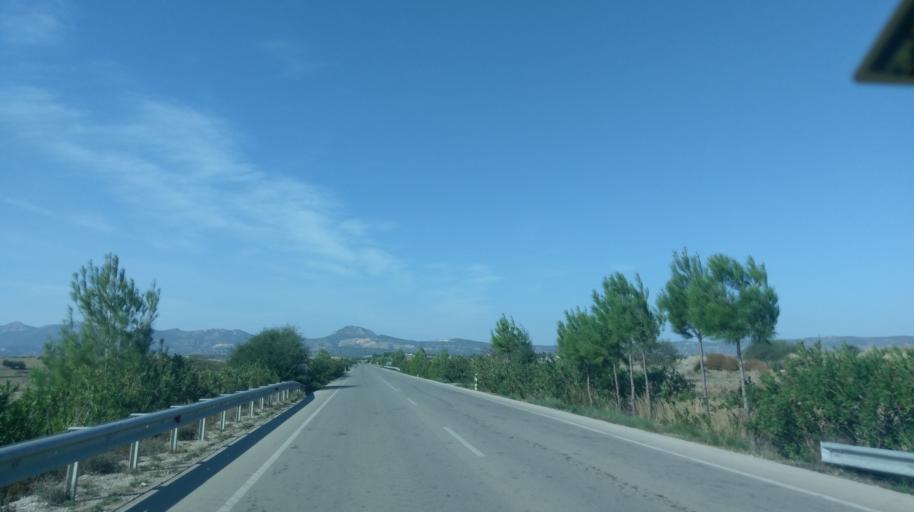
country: CY
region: Ammochostos
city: Leonarisso
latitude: 35.3791
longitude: 34.0234
